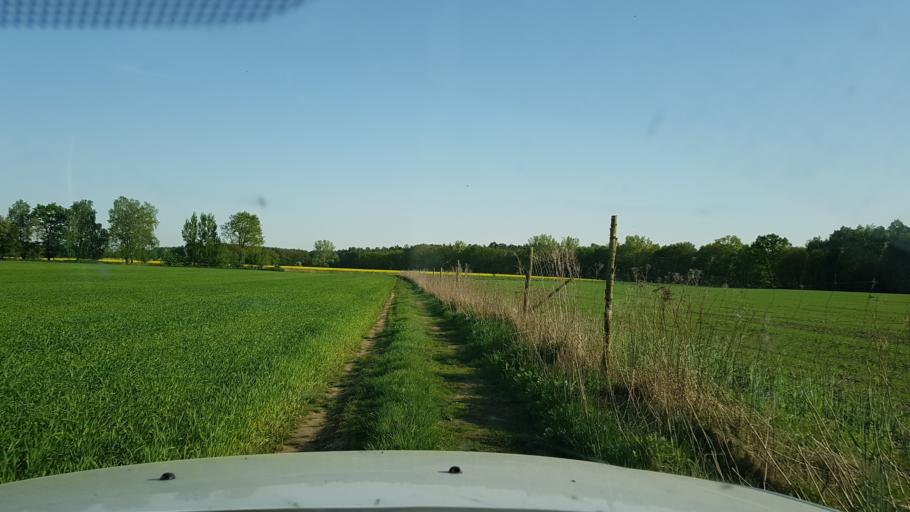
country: PL
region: West Pomeranian Voivodeship
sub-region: Powiat lobeski
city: Dobra
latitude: 53.6863
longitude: 15.3362
